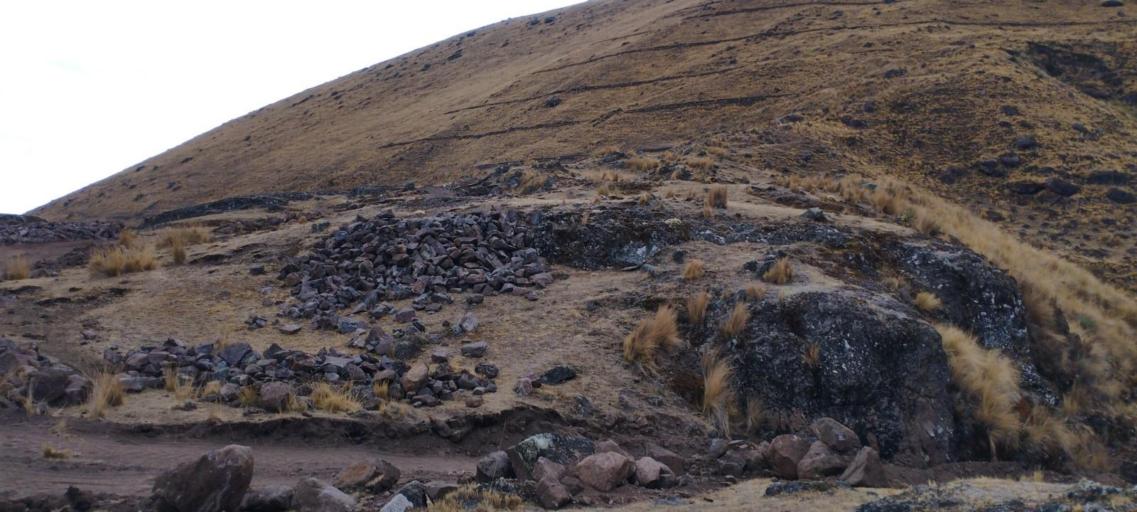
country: PE
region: Cusco
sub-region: Provincia de Calca
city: Calca
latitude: -13.2941
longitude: -71.9828
